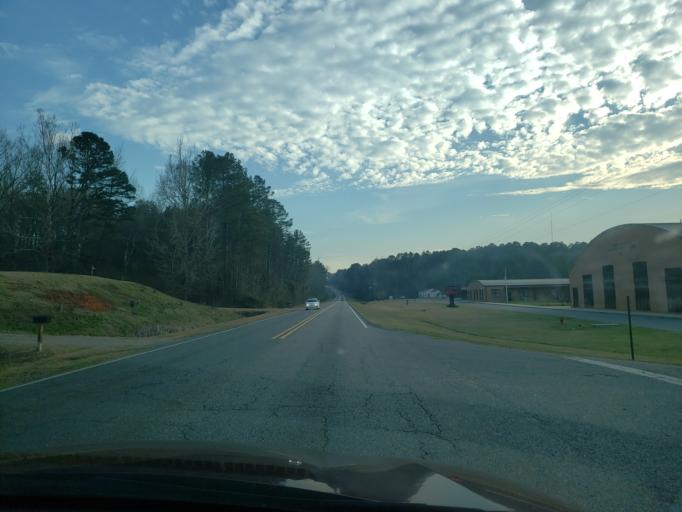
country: US
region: Alabama
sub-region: Hale County
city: Greensboro
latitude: 32.7239
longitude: -87.5911
